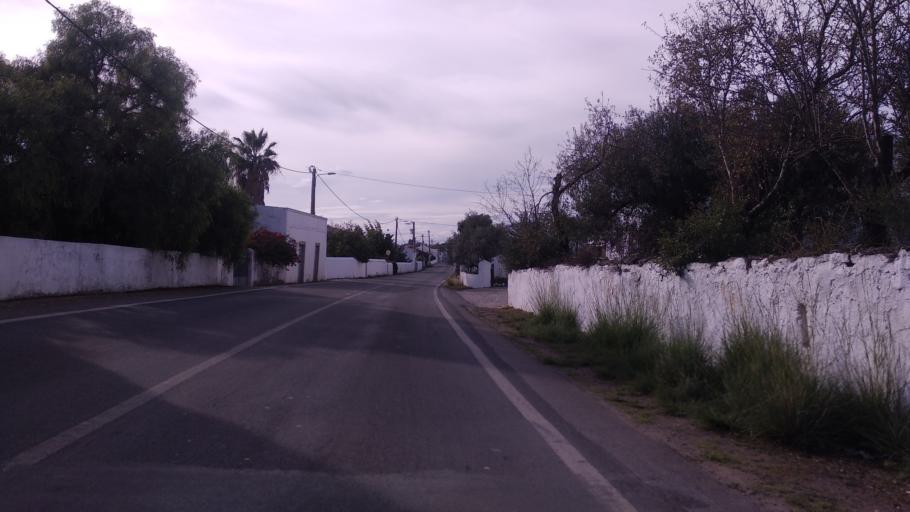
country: PT
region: Faro
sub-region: Sao Bras de Alportel
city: Sao Bras de Alportel
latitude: 37.1528
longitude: -7.9039
